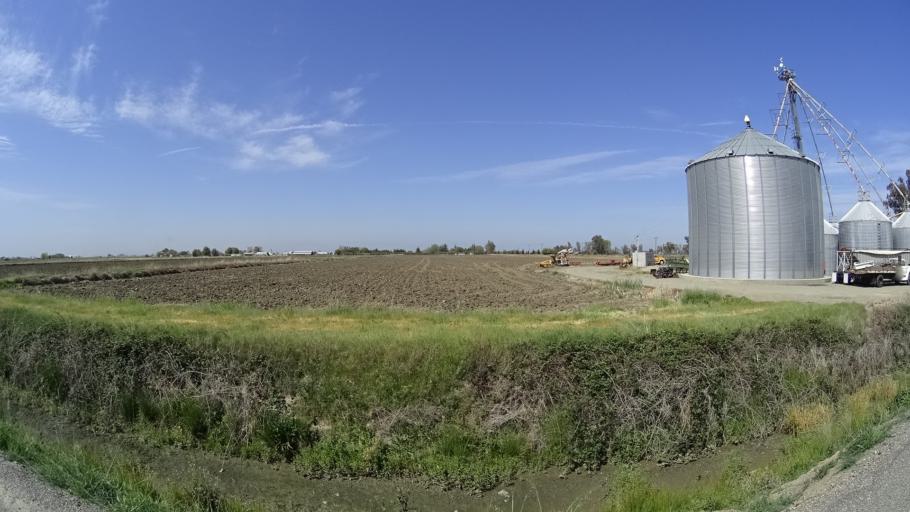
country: US
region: California
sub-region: Glenn County
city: Hamilton City
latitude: 39.5815
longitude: -122.0276
